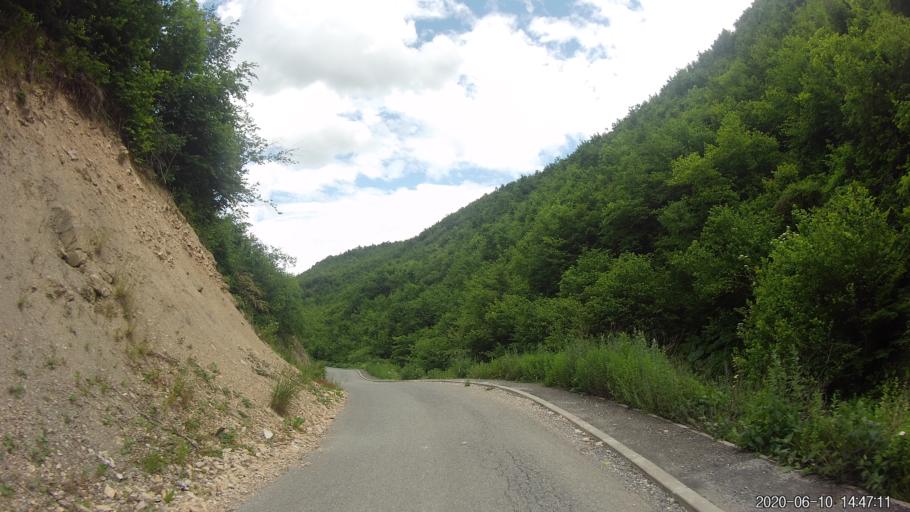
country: XK
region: Prizren
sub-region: Komuna e Therandes
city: Budakovo
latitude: 42.3864
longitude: 20.9592
